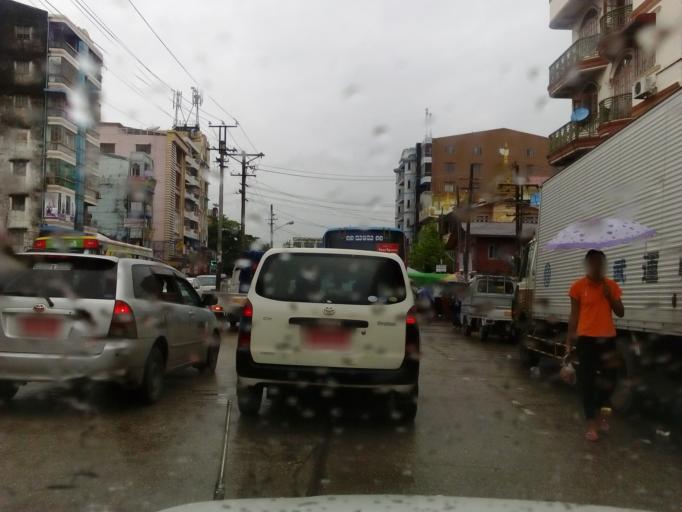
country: MM
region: Yangon
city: Yangon
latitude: 16.8080
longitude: 96.1764
